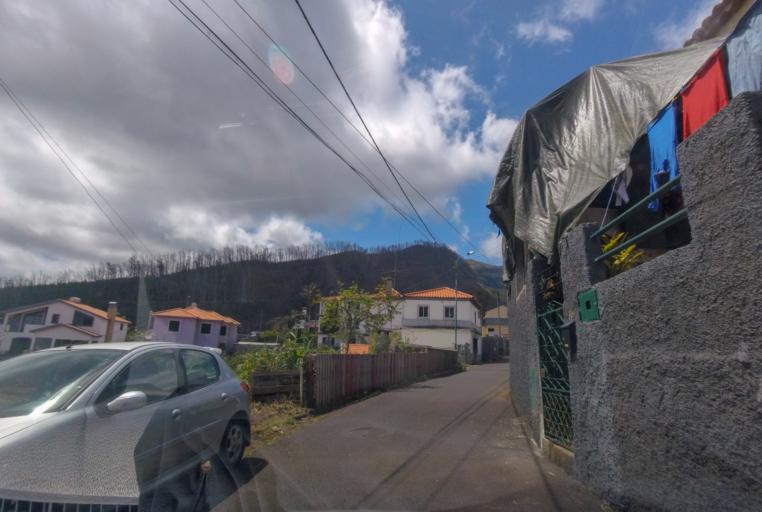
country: PT
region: Madeira
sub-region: Funchal
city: Nossa Senhora do Monte
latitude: 32.6817
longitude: -16.9126
